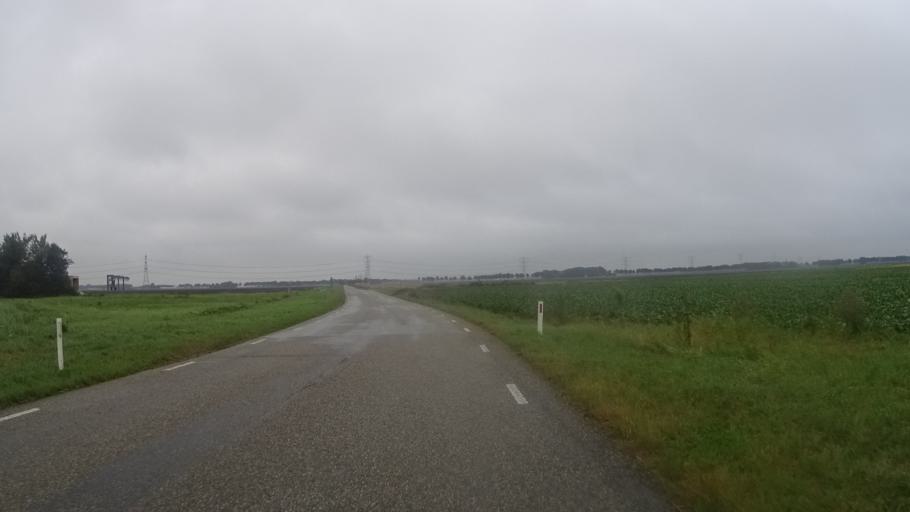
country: NL
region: Groningen
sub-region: Gemeente Veendam
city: Veendam
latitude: 53.1920
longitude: 6.9005
